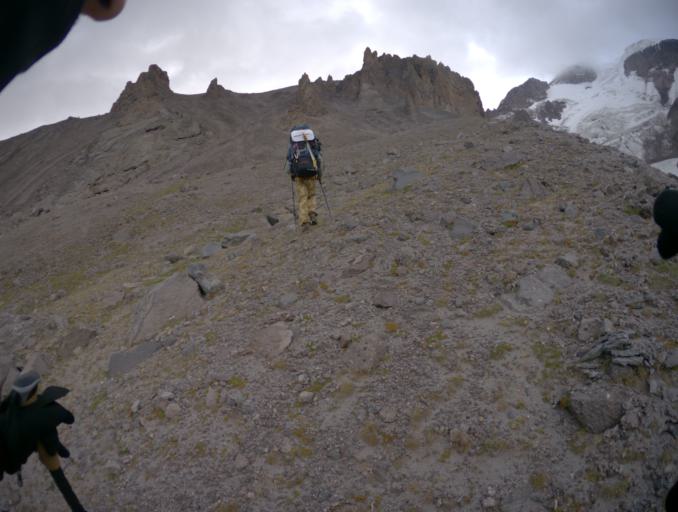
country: RU
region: Kabardino-Balkariya
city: Terskol
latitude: 43.3820
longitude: 42.3917
